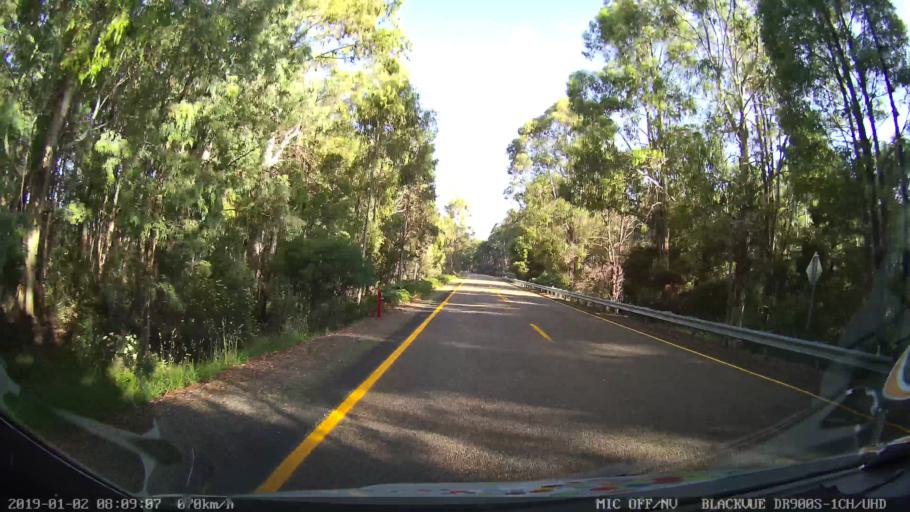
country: AU
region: New South Wales
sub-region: Tumut Shire
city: Tumut
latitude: -35.6102
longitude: 148.3812
